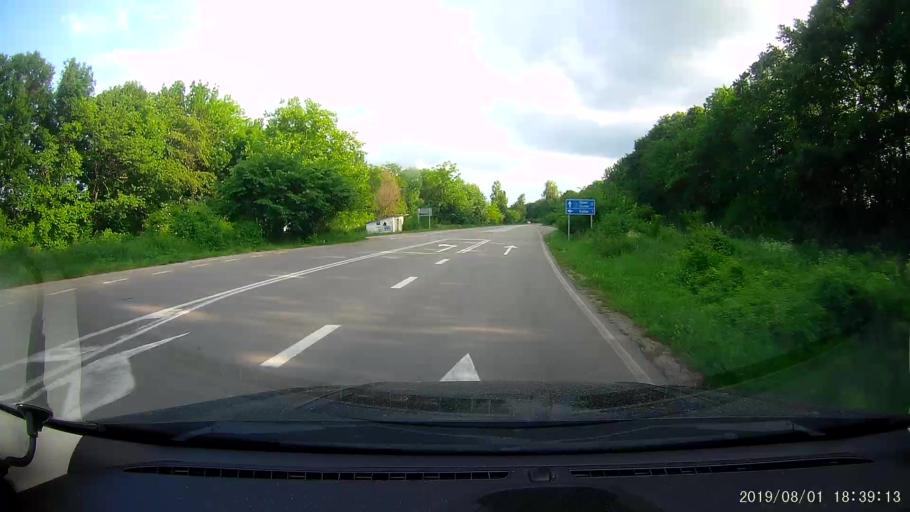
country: BG
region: Shumen
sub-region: Obshtina Khitrino
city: Gara Khitrino
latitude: 43.3899
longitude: 26.9172
